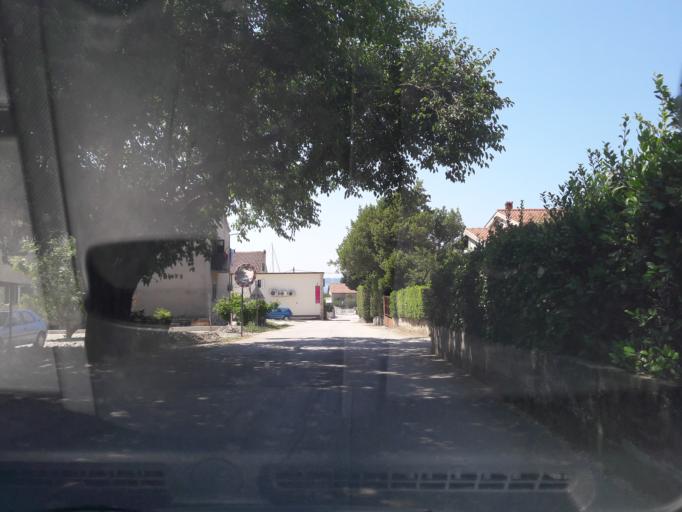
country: HR
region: Splitsko-Dalmatinska
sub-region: Grad Split
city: Split
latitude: 43.5498
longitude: 16.4002
